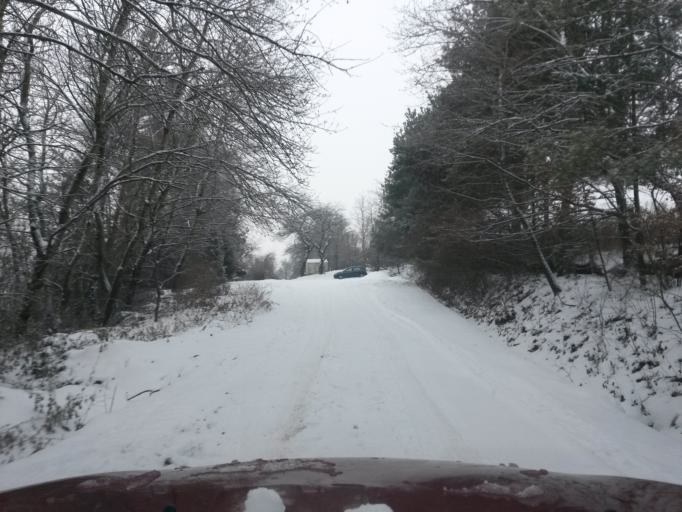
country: SK
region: Kosicky
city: Kosice
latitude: 48.7250
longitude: 21.3261
